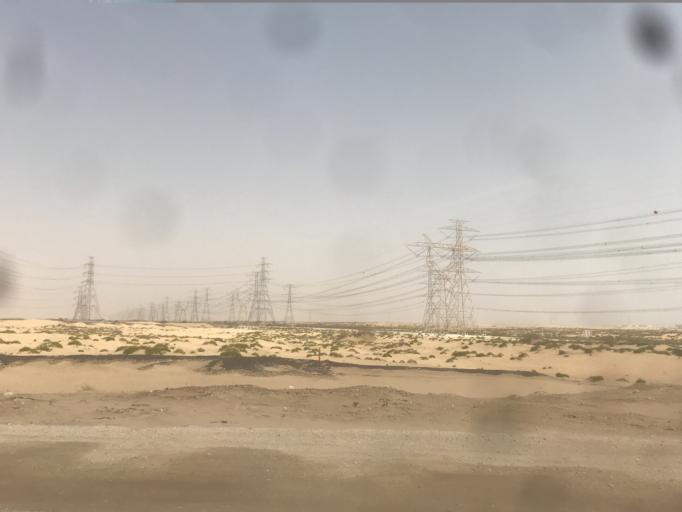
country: SA
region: Eastern Province
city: Abqaiq
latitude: 25.9067
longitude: 49.9082
